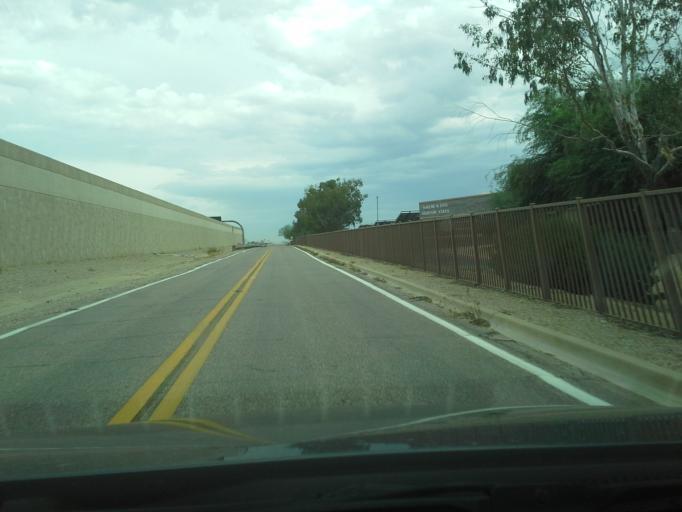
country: US
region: Arizona
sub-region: Pima County
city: Marana
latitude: 32.4552
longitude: -111.2072
